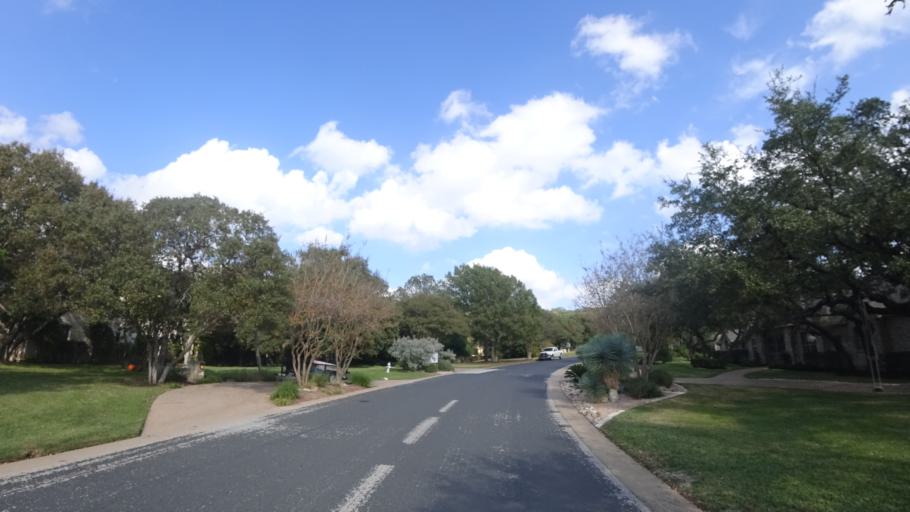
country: US
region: Texas
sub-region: Travis County
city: Lost Creek
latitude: 30.3037
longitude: -97.8452
